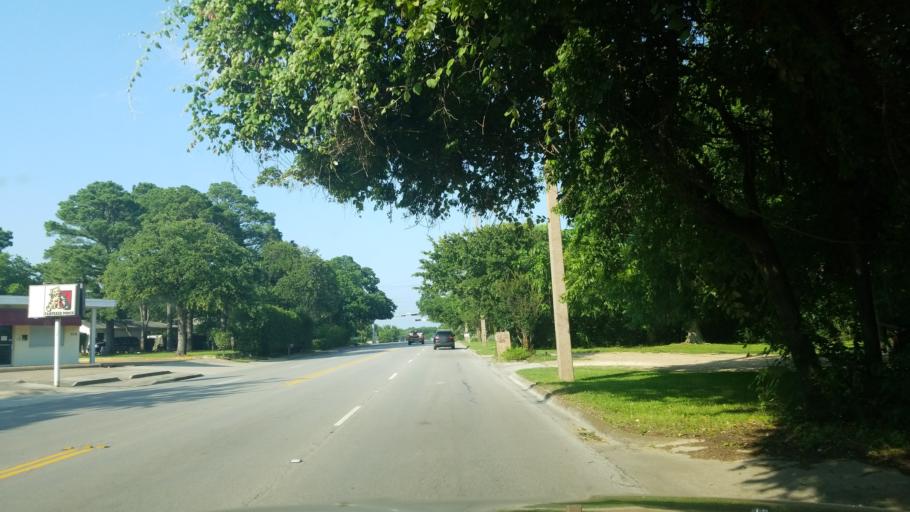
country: US
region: Texas
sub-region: Denton County
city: Denton
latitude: 33.2333
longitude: -97.1288
